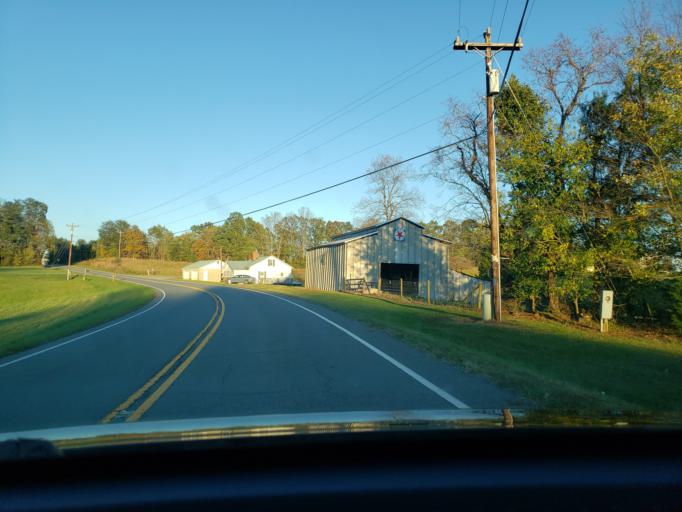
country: US
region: North Carolina
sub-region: Stokes County
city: Danbury
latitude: 36.3226
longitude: -80.2302
